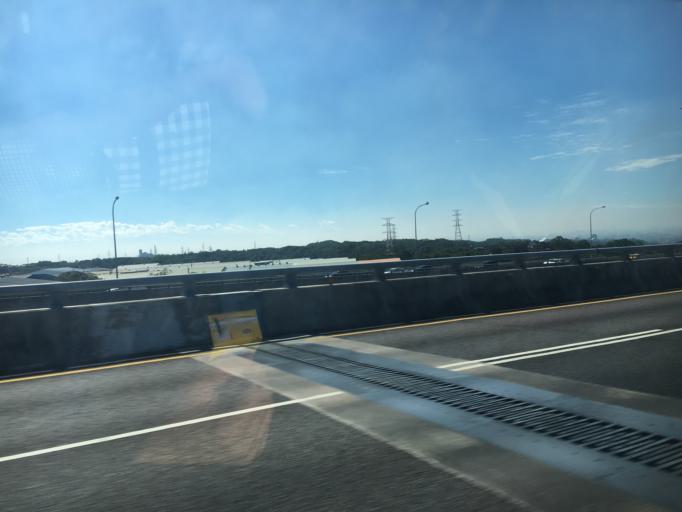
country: TW
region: Taiwan
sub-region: Taoyuan
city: Taoyuan
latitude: 25.0659
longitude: 121.3453
